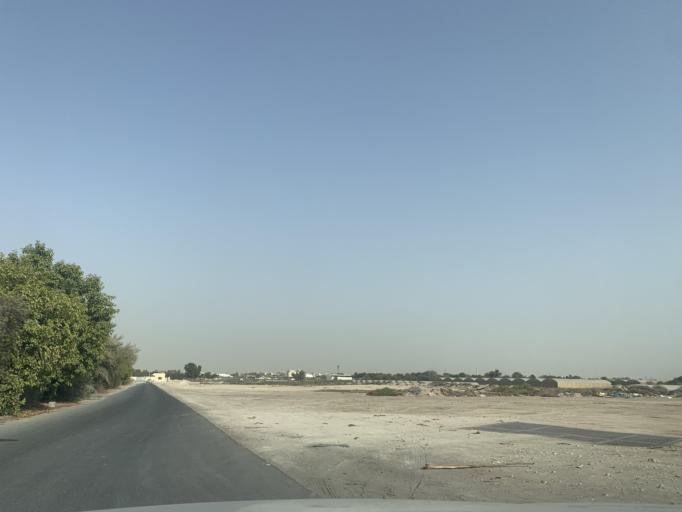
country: BH
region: Central Governorate
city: Madinat Hamad
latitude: 26.1573
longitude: 50.4881
